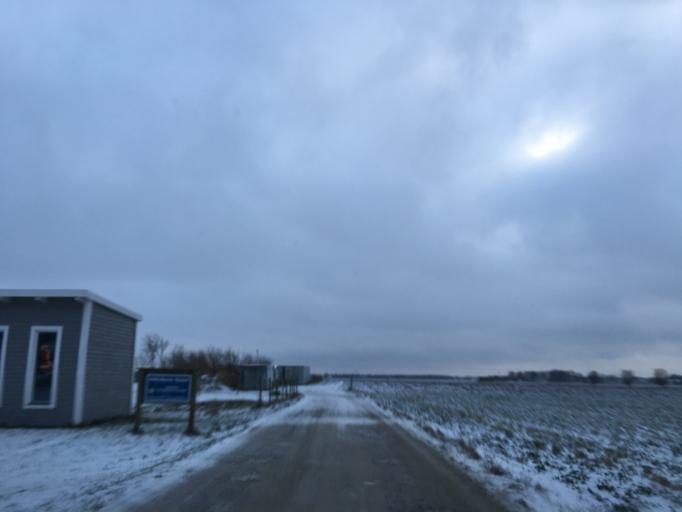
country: SE
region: Skane
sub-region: Vellinge Kommun
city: Vellinge
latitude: 55.4384
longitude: 12.9978
